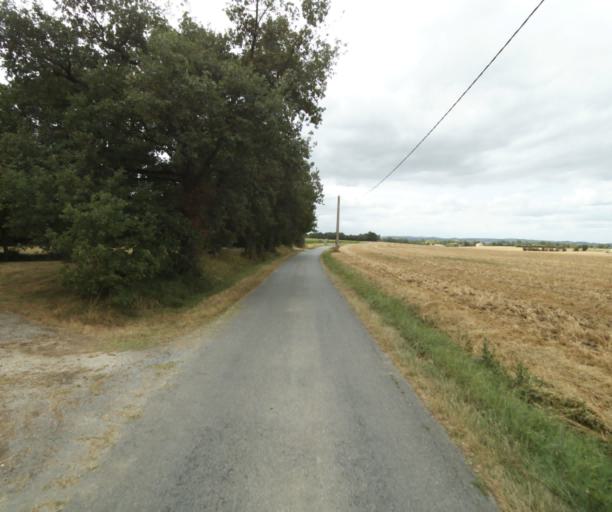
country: FR
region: Midi-Pyrenees
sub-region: Departement du Tarn
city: Soreze
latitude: 43.4808
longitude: 2.0628
